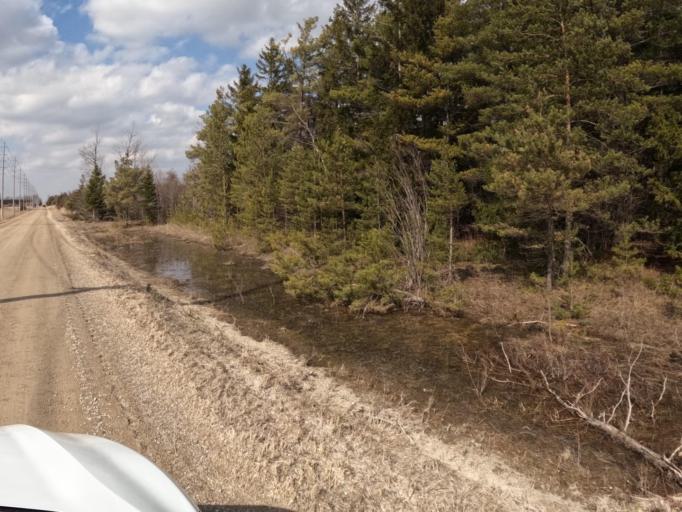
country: CA
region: Ontario
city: Shelburne
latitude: 43.9632
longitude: -80.2997
